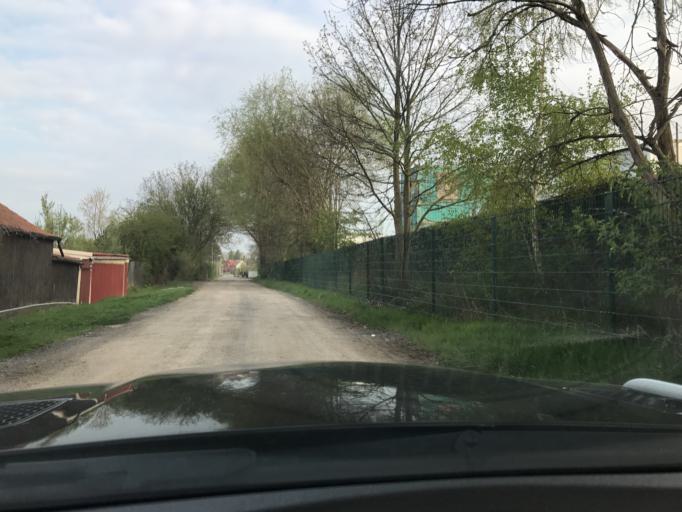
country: DE
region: Thuringia
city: Muehlhausen
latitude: 51.2075
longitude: 10.4811
